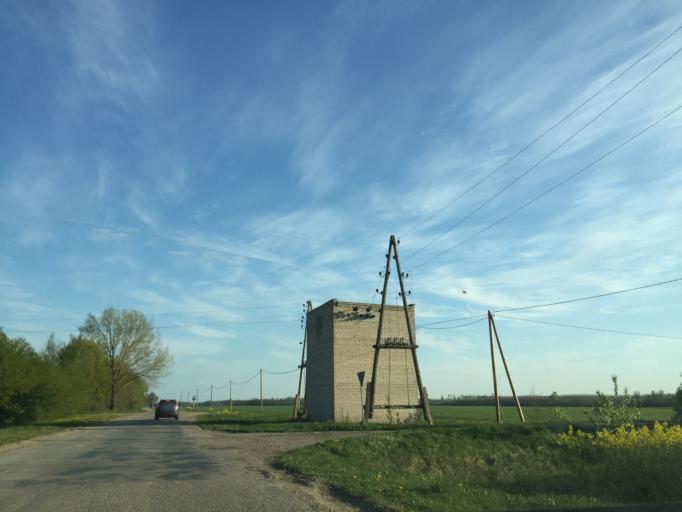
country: LV
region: Bauskas Rajons
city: Bauska
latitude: 56.2972
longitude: 24.2609
